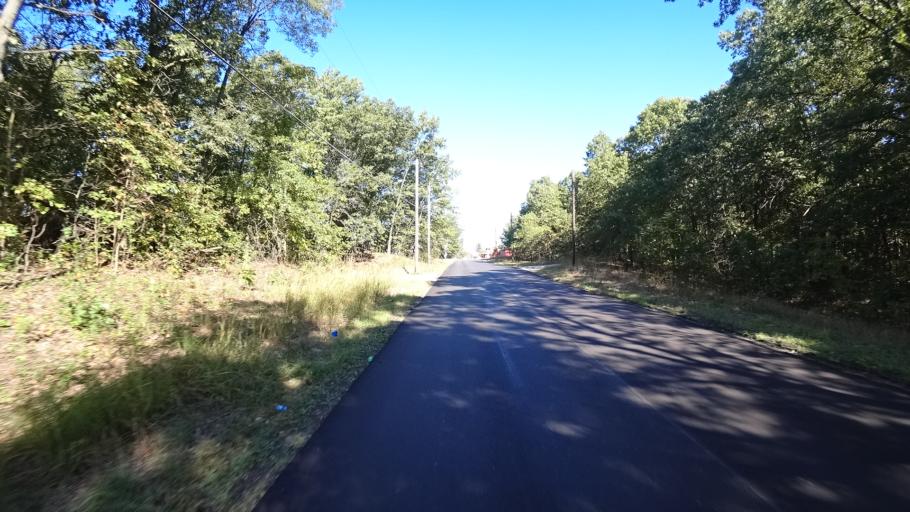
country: US
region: Indiana
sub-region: LaPorte County
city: Michigan City
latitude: 41.6996
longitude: -86.9140
